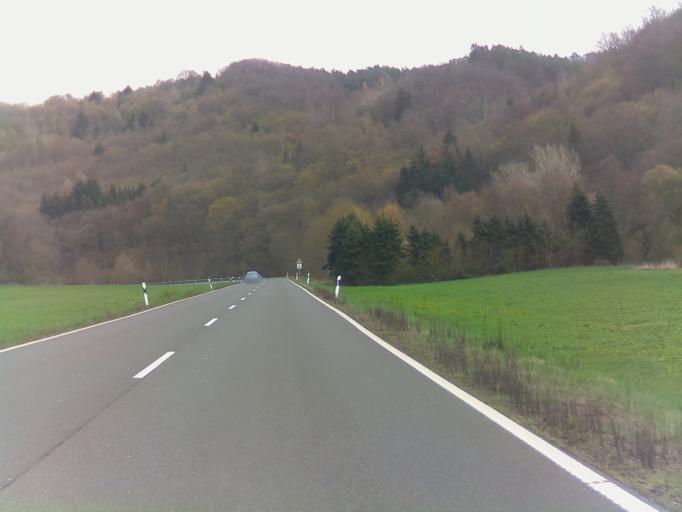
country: DE
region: Rheinland-Pfalz
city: Kellenbach
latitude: 49.8399
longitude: 7.4897
